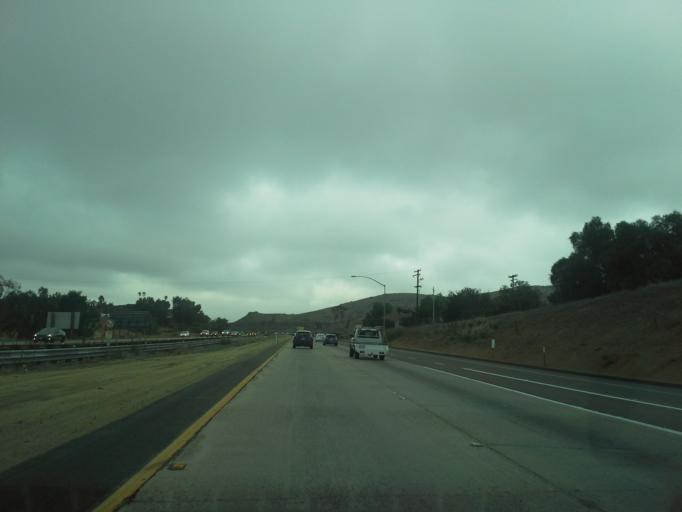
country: US
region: California
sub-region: San Diego County
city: Granite Hills
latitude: 32.8145
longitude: -116.9150
